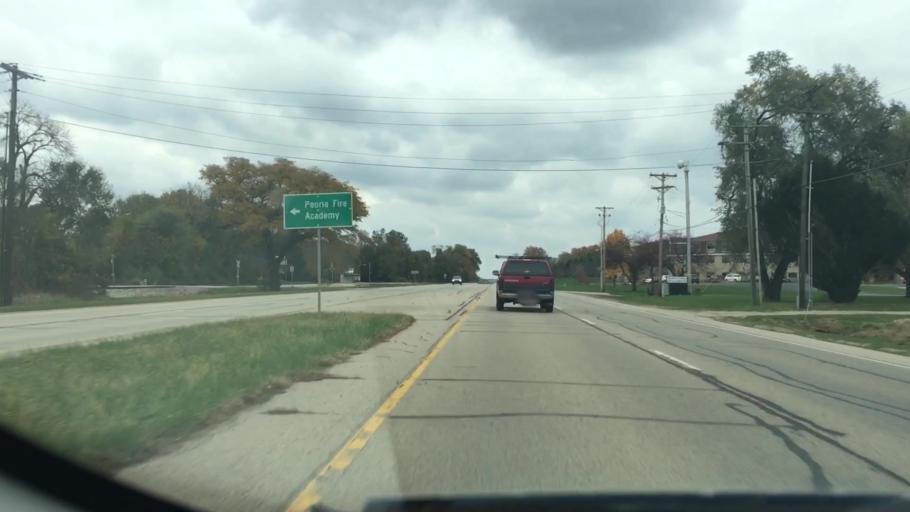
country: US
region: Illinois
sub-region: Peoria County
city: Peoria Heights
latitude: 40.7734
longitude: -89.5745
